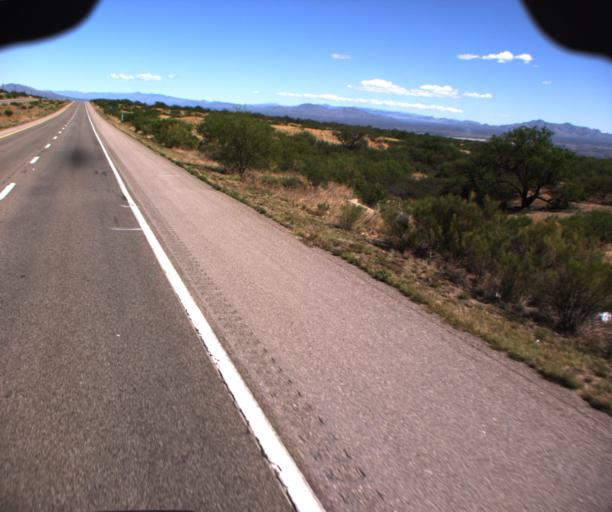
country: US
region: Arizona
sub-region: Cochise County
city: Whetstone
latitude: 31.8853
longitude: -110.3410
